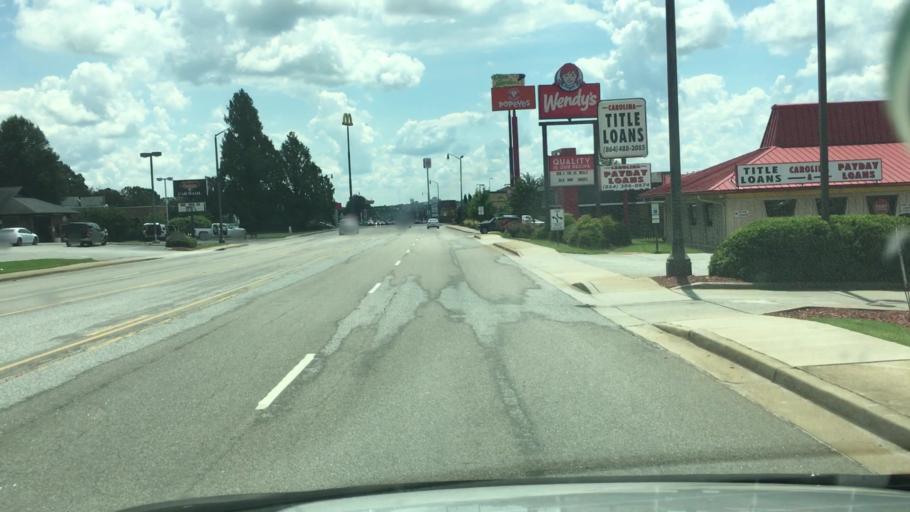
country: US
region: South Carolina
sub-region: Cherokee County
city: Gaffney
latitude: 35.0946
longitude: -81.6664
